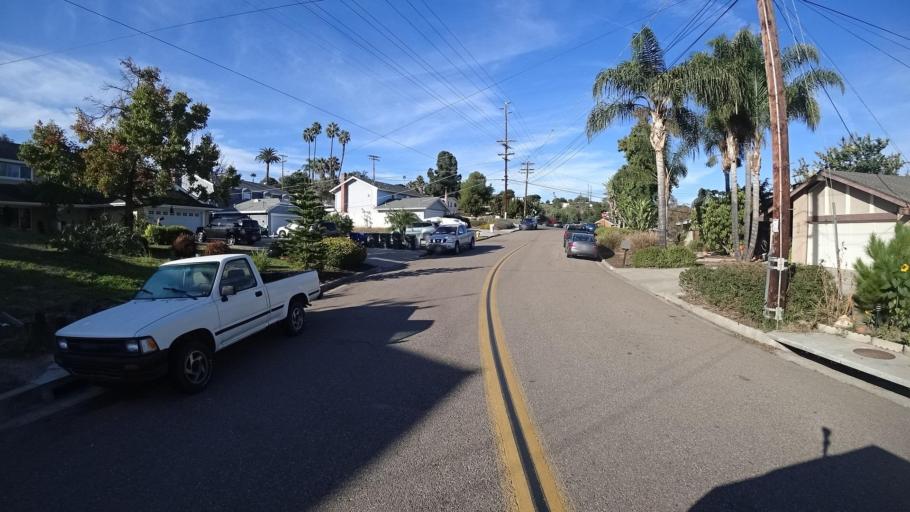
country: US
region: California
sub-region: San Diego County
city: Spring Valley
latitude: 32.7408
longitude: -116.9804
